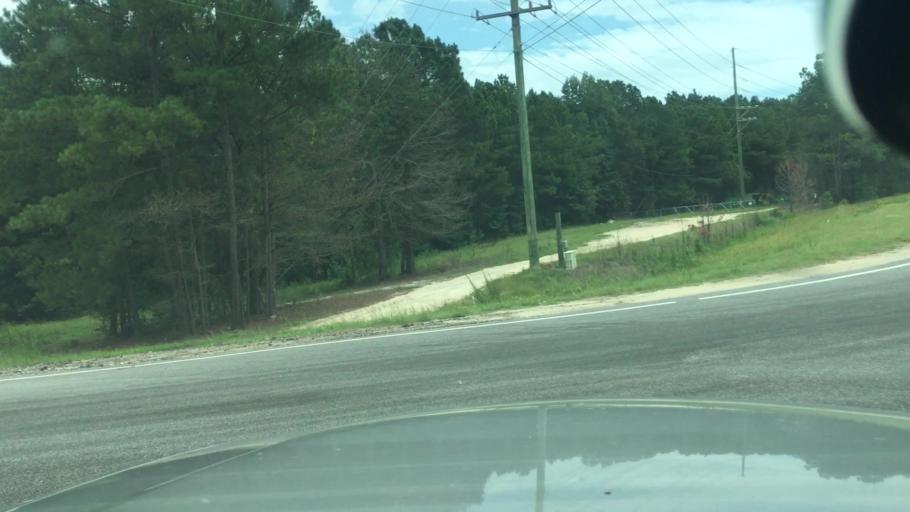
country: US
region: North Carolina
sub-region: Cumberland County
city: Hope Mills
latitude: 34.9595
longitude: -78.9010
